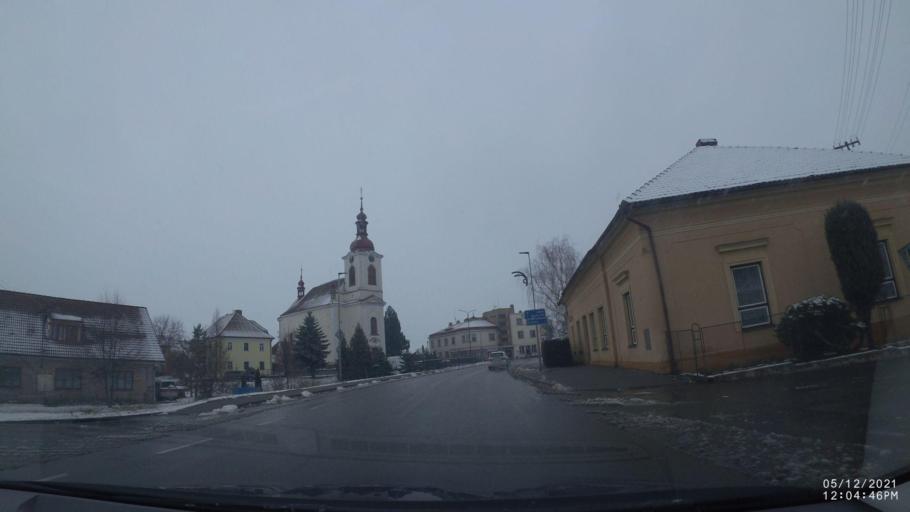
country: CZ
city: Ceske Mezirici
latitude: 50.2863
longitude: 16.0454
